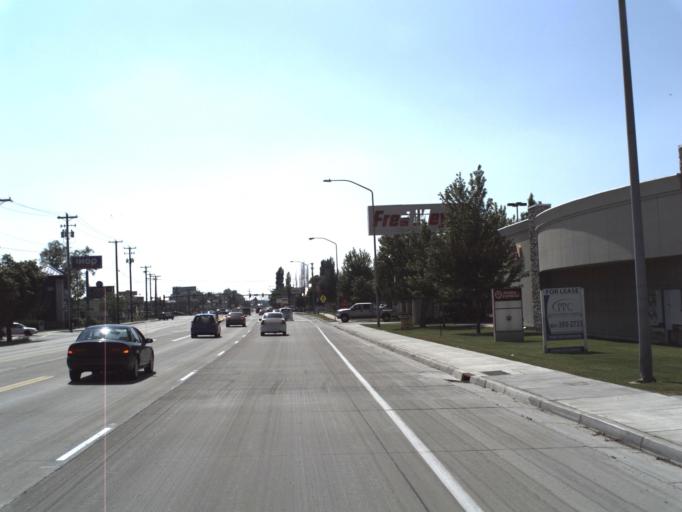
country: US
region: Utah
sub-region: Weber County
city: Ogden
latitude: 41.2444
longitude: -111.9713
